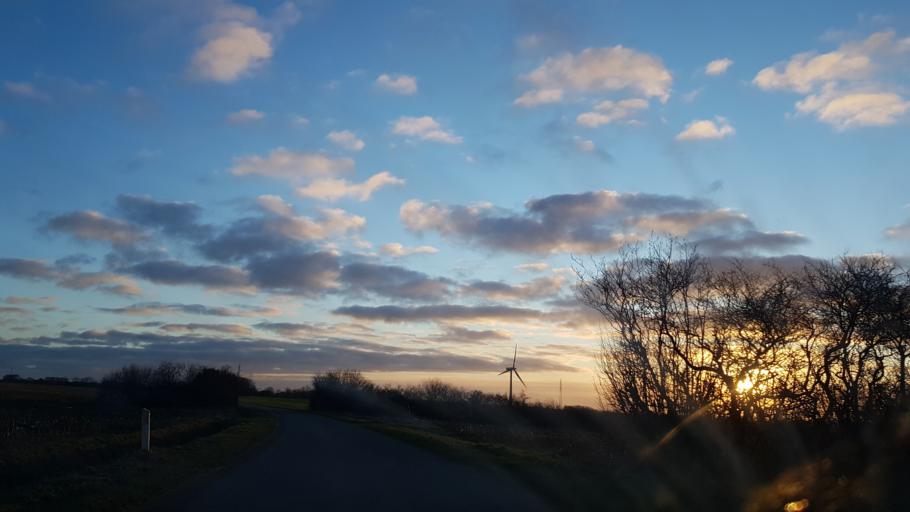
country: DK
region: South Denmark
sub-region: Kolding Kommune
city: Vamdrup
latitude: 55.3524
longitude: 9.2791
